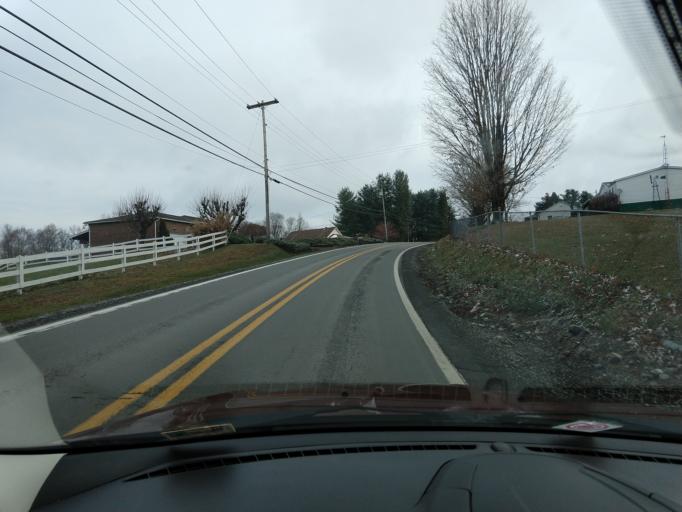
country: US
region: West Virginia
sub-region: Nicholas County
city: Craigsville
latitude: 38.2078
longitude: -80.6821
